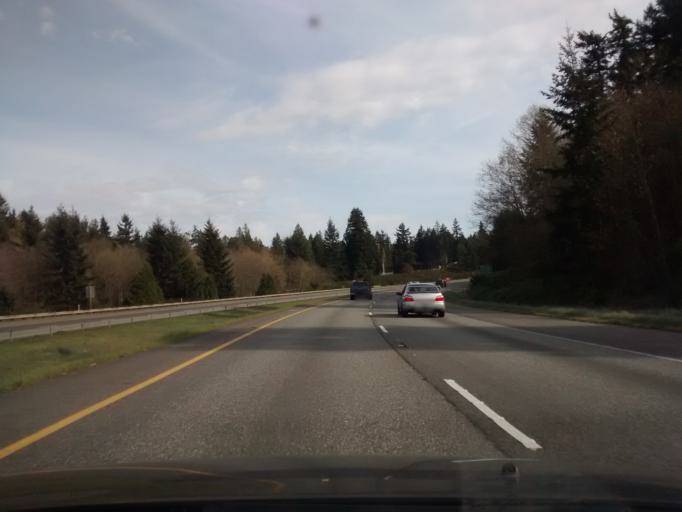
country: US
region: Washington
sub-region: Kitsap County
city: Silverdale
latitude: 47.6559
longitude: -122.7051
